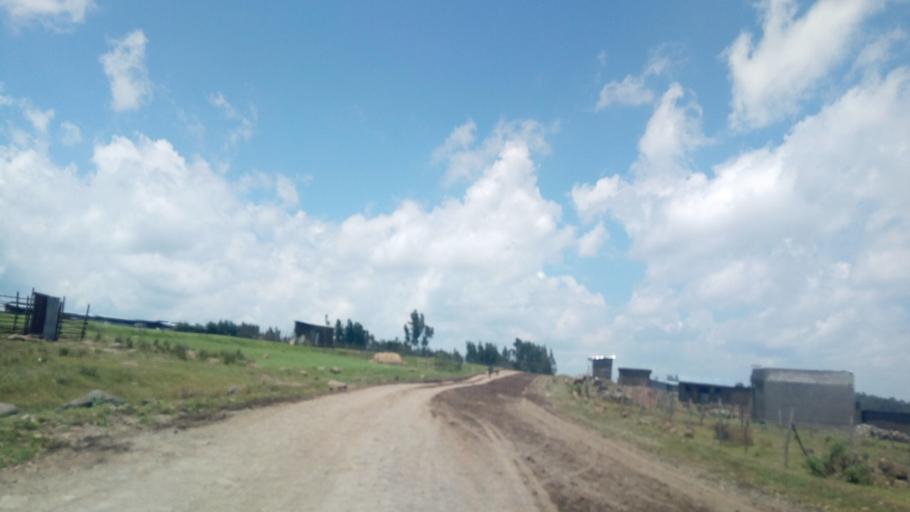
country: ET
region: Oromiya
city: Sendafa
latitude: 8.9758
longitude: 39.1202
